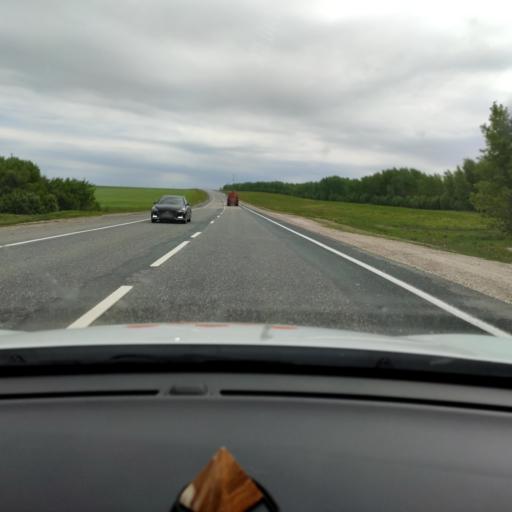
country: RU
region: Tatarstan
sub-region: Alekseyevskiy Rayon
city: Alekseyevskoye
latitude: 55.3832
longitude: 49.9047
